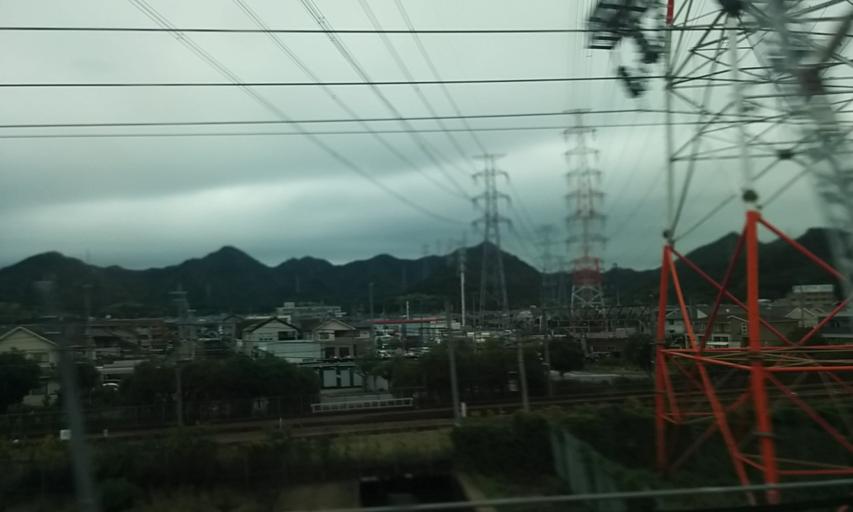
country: JP
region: Hyogo
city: Shirahamacho-usazakiminami
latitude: 34.8097
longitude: 134.7455
